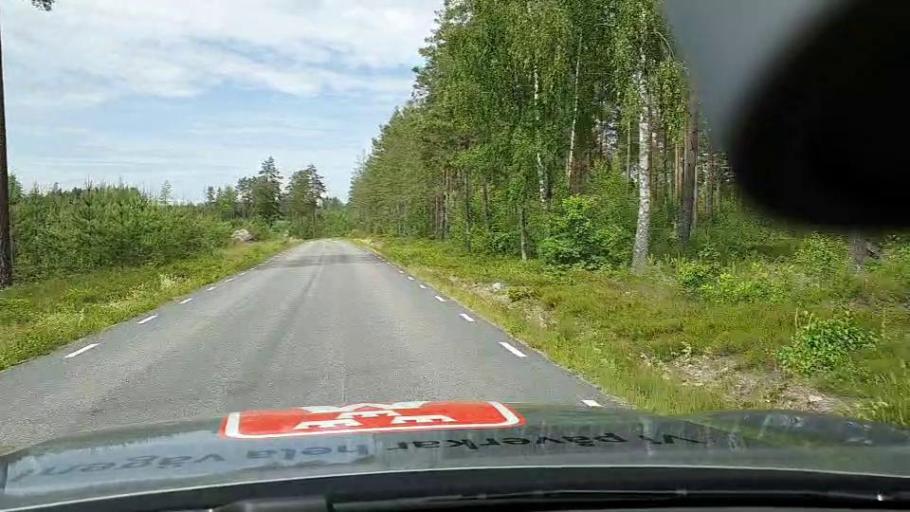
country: SE
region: Soedermanland
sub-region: Eskilstuna Kommun
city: Arla
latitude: 59.2353
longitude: 16.7231
